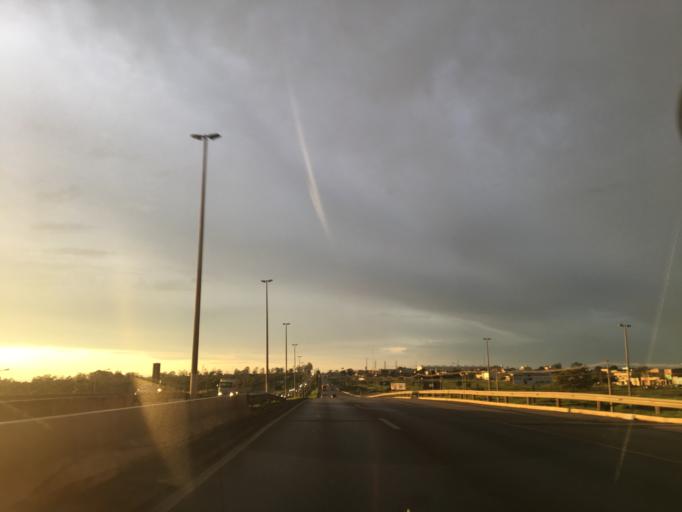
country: BR
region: Federal District
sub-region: Brasilia
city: Brasilia
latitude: -16.0033
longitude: -47.9841
